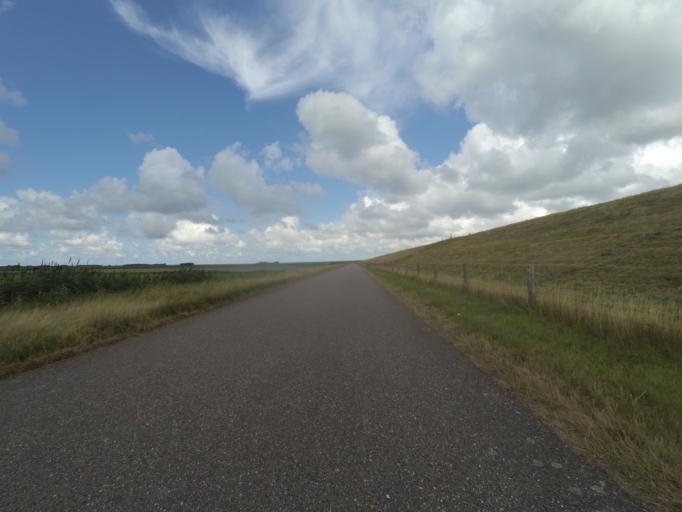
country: NL
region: North Holland
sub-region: Gemeente Texel
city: Den Burg
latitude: 53.1331
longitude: 4.9004
